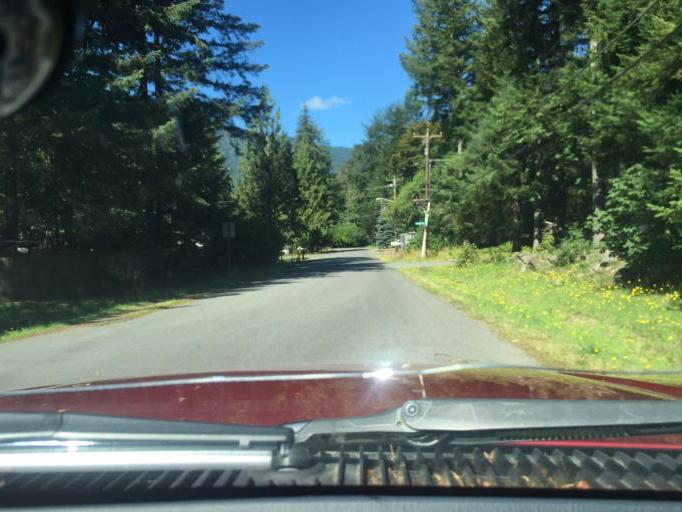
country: US
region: Washington
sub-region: King County
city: Riverbend
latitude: 47.4681
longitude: -121.7473
